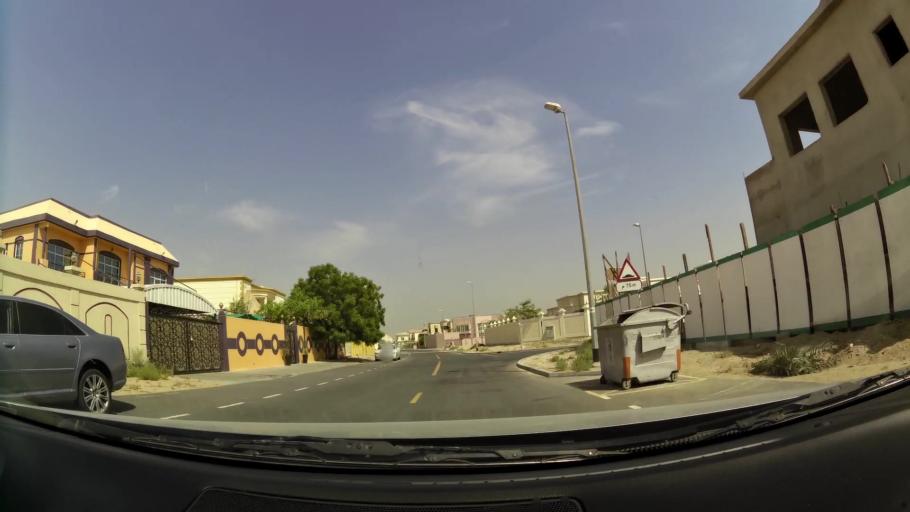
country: AE
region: Ash Shariqah
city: Sharjah
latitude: 25.1987
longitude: 55.4211
